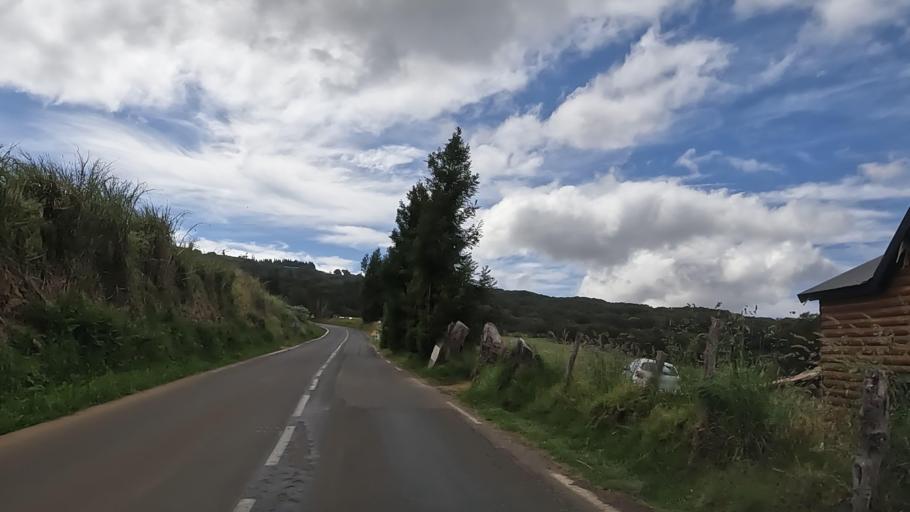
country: RE
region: Reunion
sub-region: Reunion
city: Le Tampon
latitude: -21.2370
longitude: 55.5819
